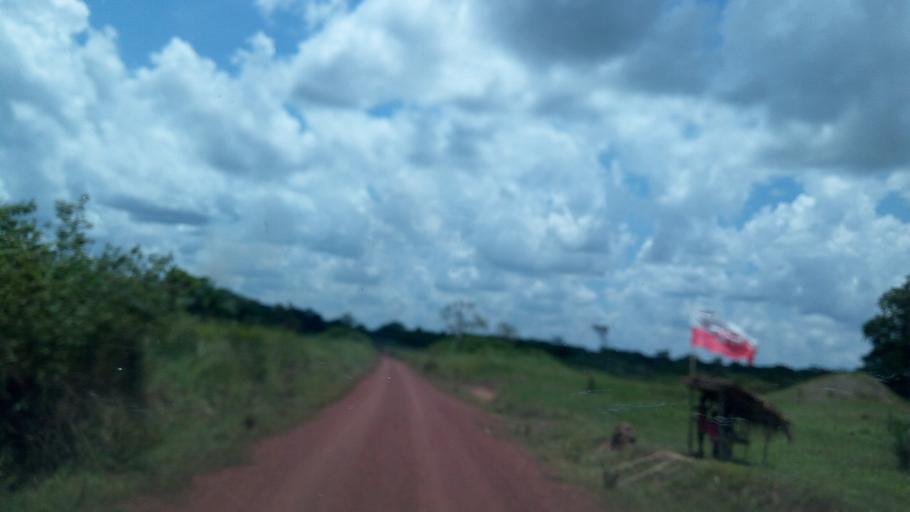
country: CD
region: Equateur
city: Libenge
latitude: 3.7715
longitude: 18.9516
